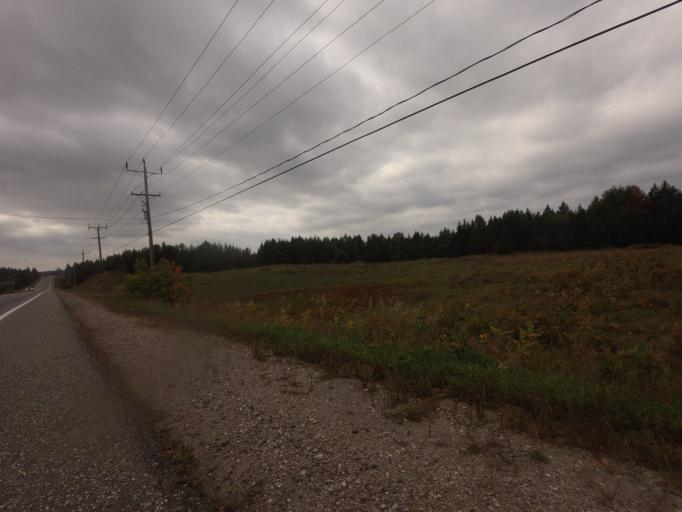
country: CA
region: Quebec
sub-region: Outaouais
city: Wakefield
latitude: 45.9234
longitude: -76.0172
